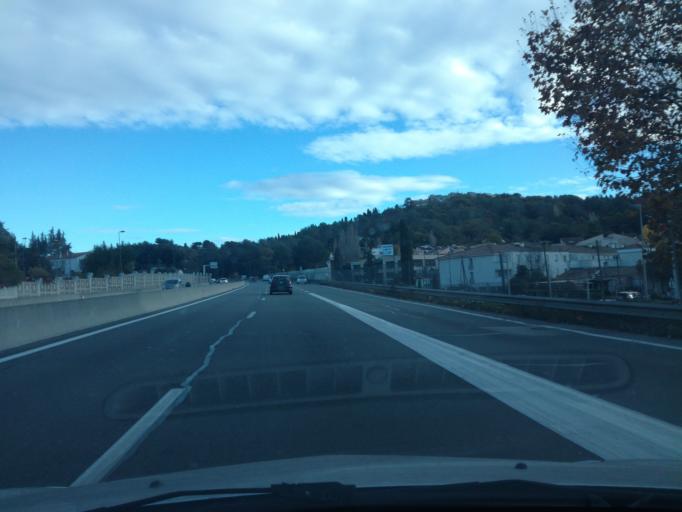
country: FR
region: Provence-Alpes-Cote d'Azur
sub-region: Departement des Alpes-Maritimes
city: Mougins
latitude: 43.6060
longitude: 6.9883
